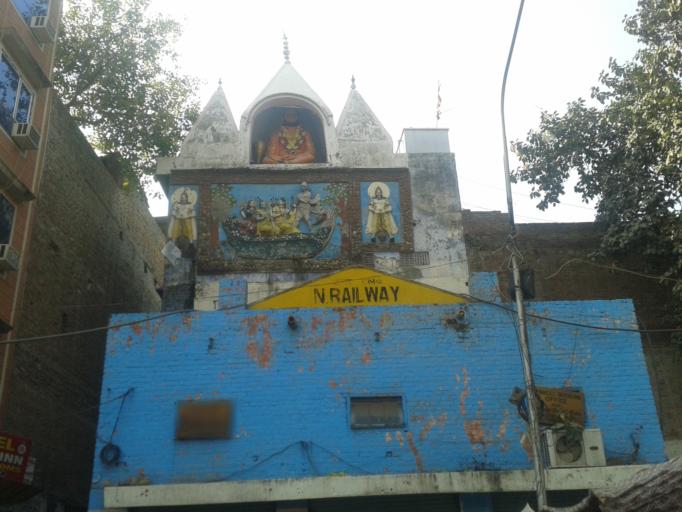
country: IN
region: Punjab
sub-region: Amritsar
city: Amritsar
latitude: 31.6250
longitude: 74.8785
